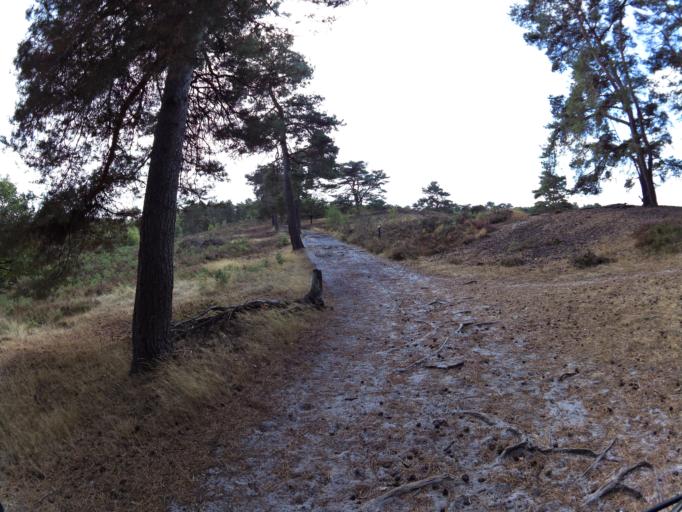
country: NL
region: Limburg
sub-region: Gemeente Brunssum
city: Brunssum
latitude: 50.9214
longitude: 5.9949
